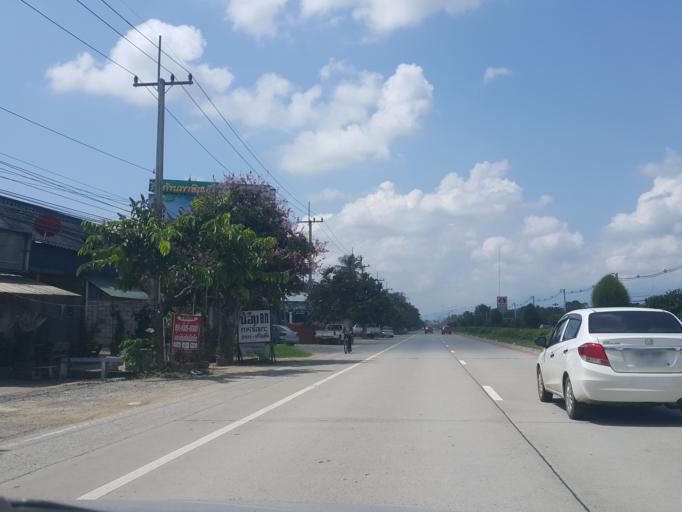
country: TH
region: Chiang Mai
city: San Sai
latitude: 18.8559
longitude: 99.0992
